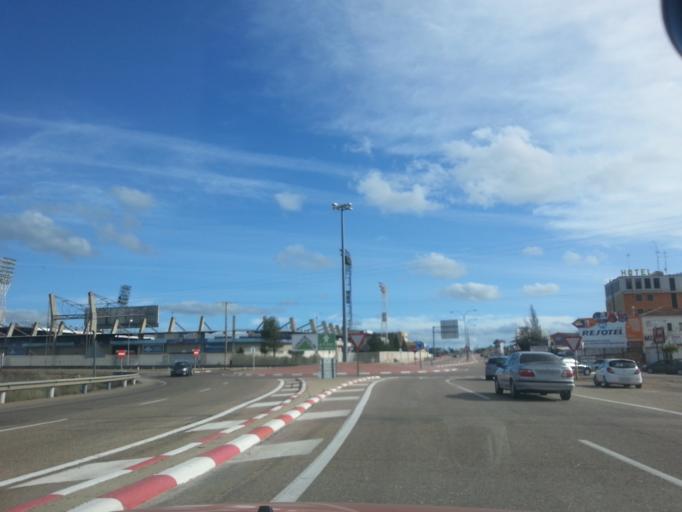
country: ES
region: Castille and Leon
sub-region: Provincia de Salamanca
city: Villares de la Reina
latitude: 40.9972
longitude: -5.6665
